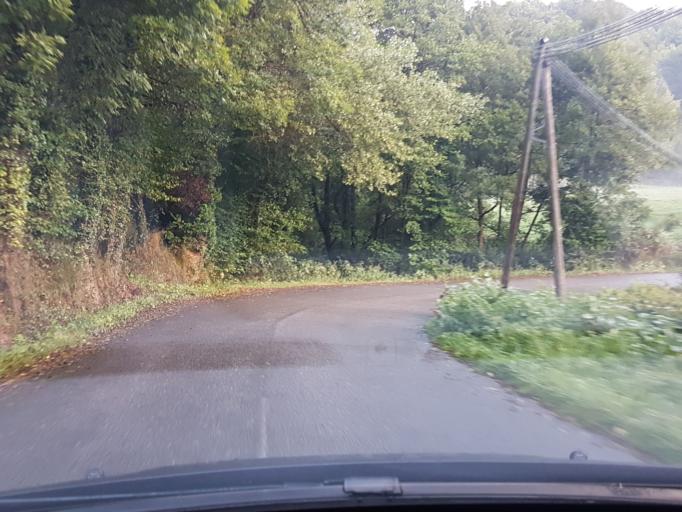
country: FR
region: Midi-Pyrenees
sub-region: Departement de l'Ariege
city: Montjoie-en-Couserans
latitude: 42.9048
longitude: 1.3689
